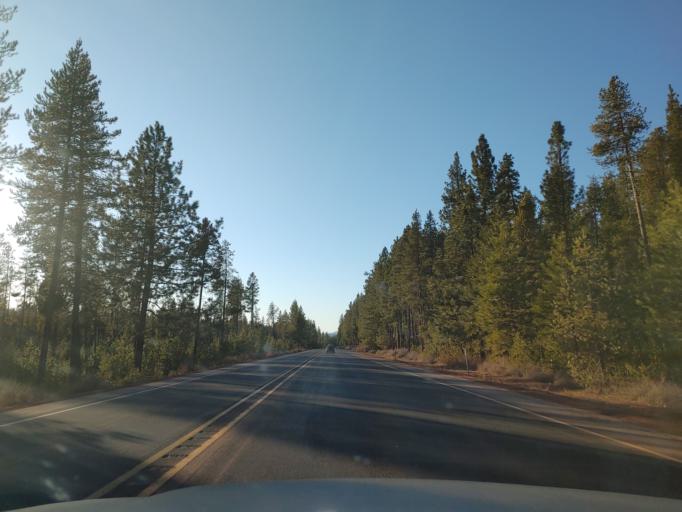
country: US
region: Oregon
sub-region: Deschutes County
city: La Pine
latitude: 43.4580
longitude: -121.8788
